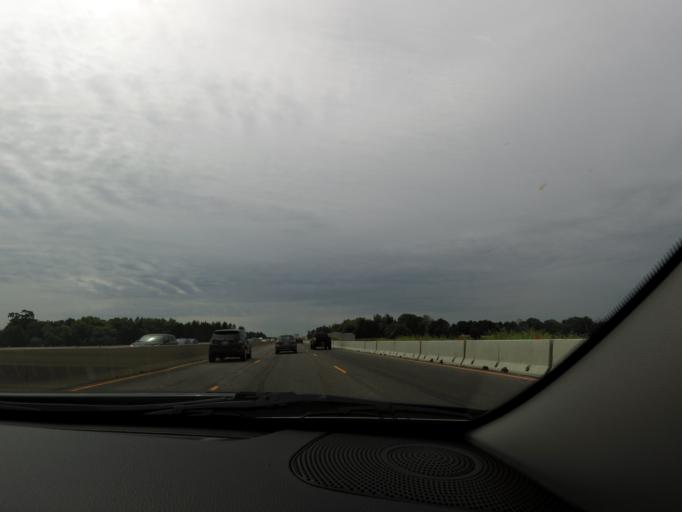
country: CA
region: Ontario
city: Bradford West Gwillimbury
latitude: 44.0136
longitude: -79.5901
